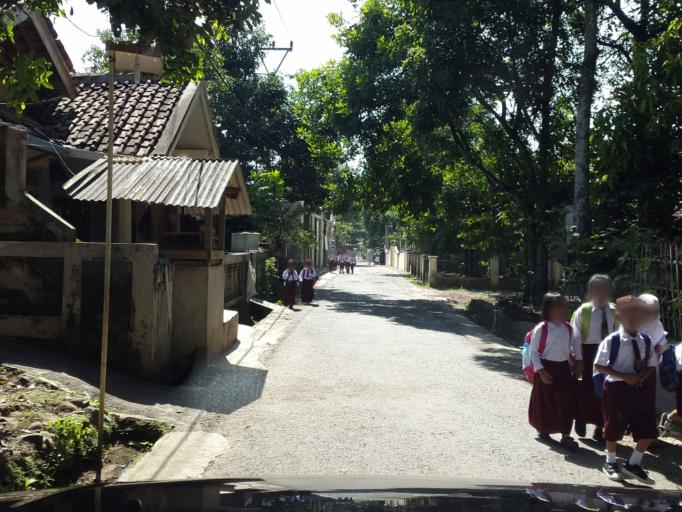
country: ID
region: West Java
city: Ciranjang-hilir
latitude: -6.7892
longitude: 107.1998
